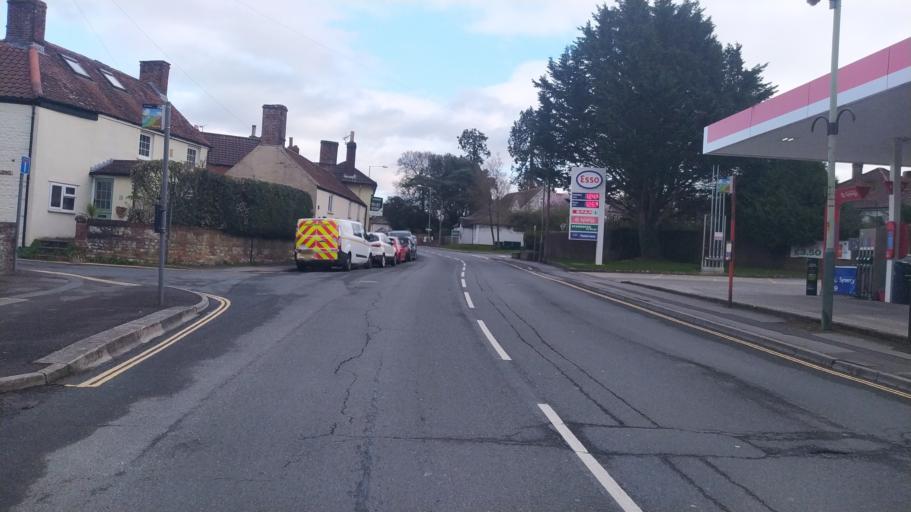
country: GB
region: England
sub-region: Wiltshire
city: Warminster
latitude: 51.2032
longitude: -2.1764
